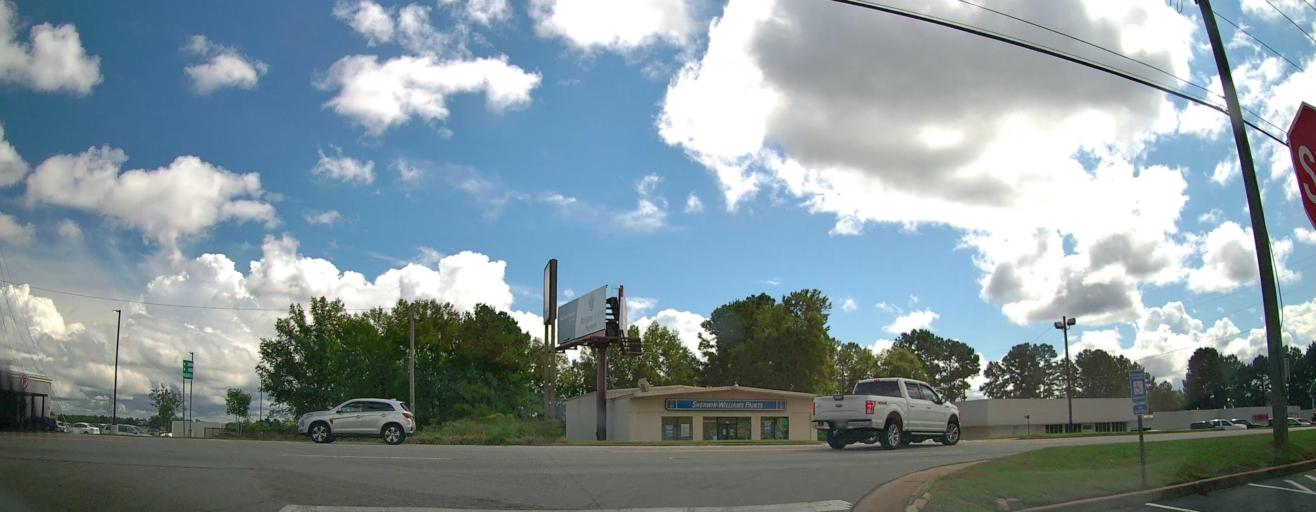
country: US
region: Georgia
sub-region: Baldwin County
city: Milledgeville
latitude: 33.1075
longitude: -83.2573
